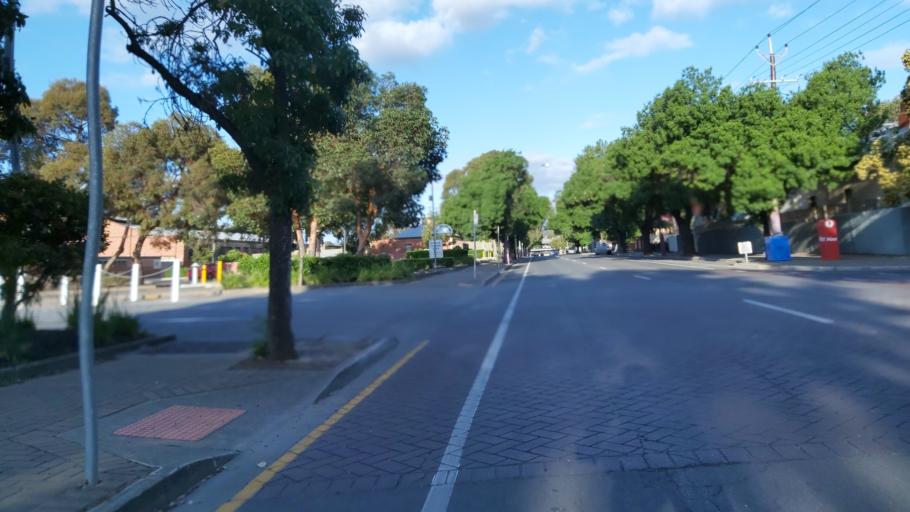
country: AU
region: South Australia
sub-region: Unley
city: Wayville
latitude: -34.9488
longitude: 138.5854
